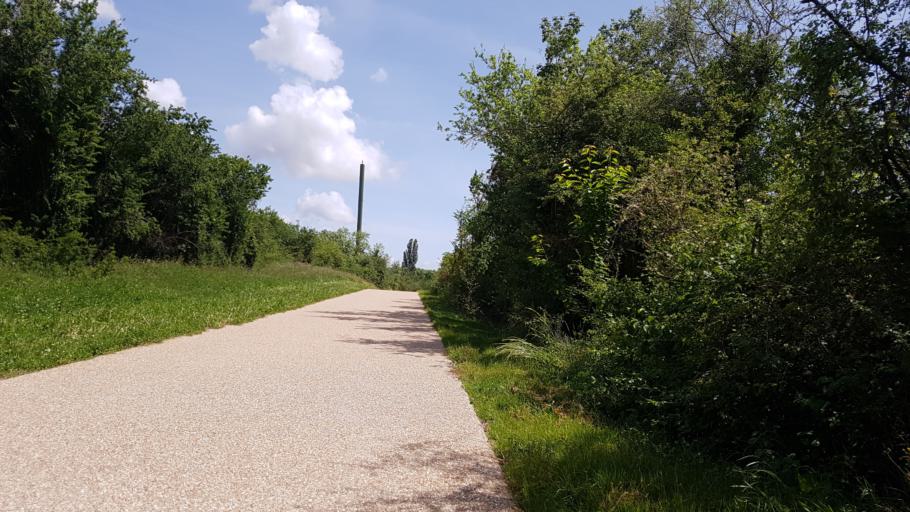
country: FR
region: Rhone-Alpes
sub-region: Departement du Rhone
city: Sathonay-Camp
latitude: 45.8172
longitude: 4.8775
